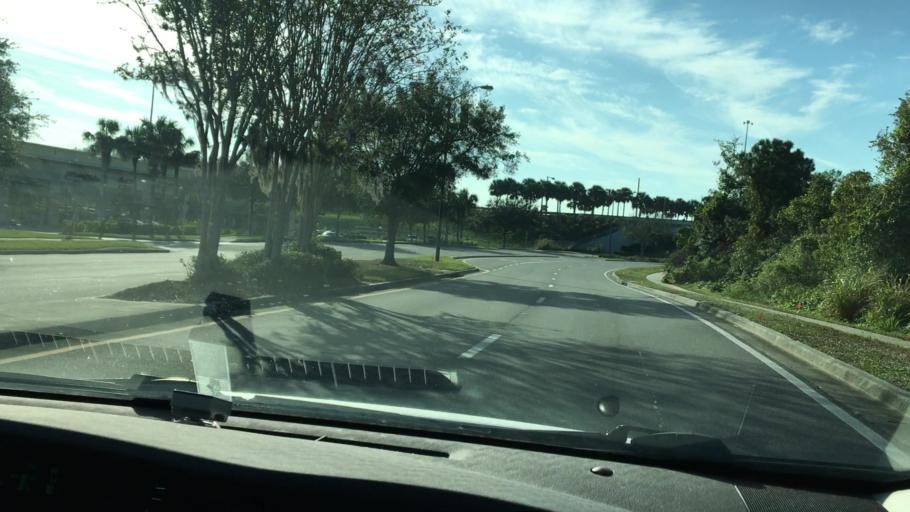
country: US
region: Florida
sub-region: Seminole County
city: Lake Mary
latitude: 28.7984
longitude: -81.3391
